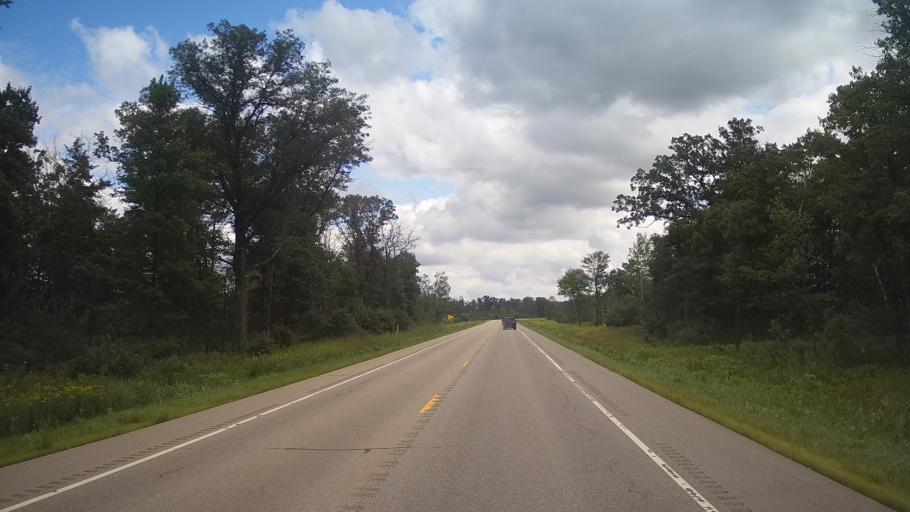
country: US
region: Wisconsin
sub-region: Adams County
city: Friendship
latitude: 44.0258
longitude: -89.6918
